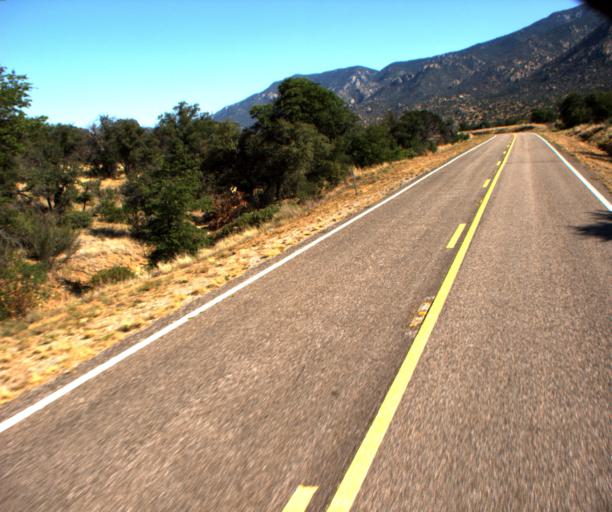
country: US
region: Arizona
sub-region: Graham County
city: Swift Trail Junction
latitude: 32.5891
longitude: -109.8544
